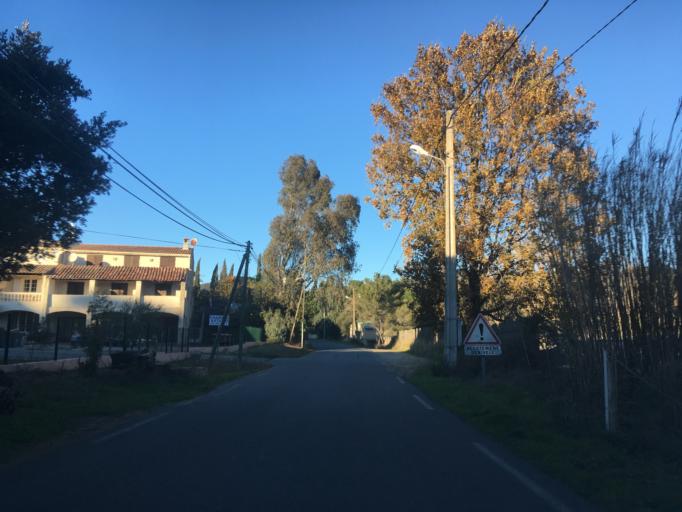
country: FR
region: Provence-Alpes-Cote d'Azur
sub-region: Departement du Var
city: Grimaud
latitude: 43.2840
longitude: 6.5762
